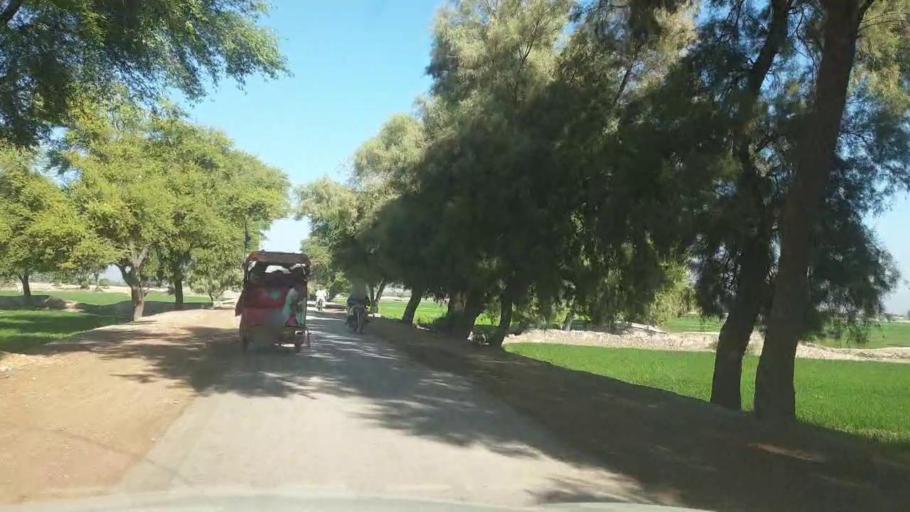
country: PK
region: Sindh
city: Bhan
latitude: 26.5520
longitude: 67.6336
